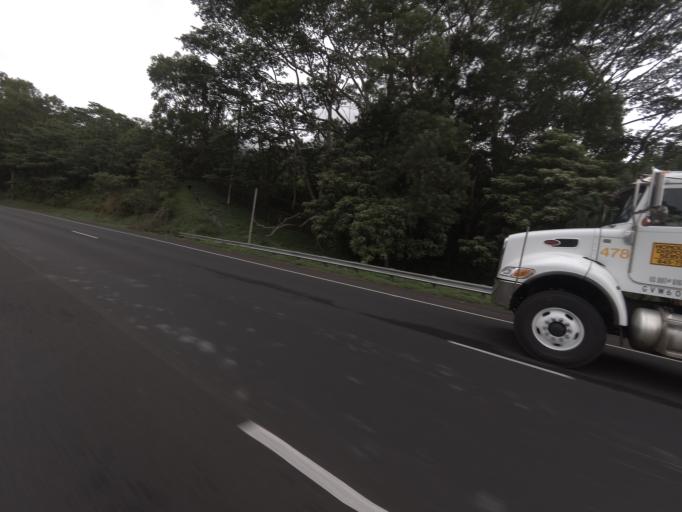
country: US
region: Hawaii
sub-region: Honolulu County
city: Kane'ohe
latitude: 21.3995
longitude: -157.8101
